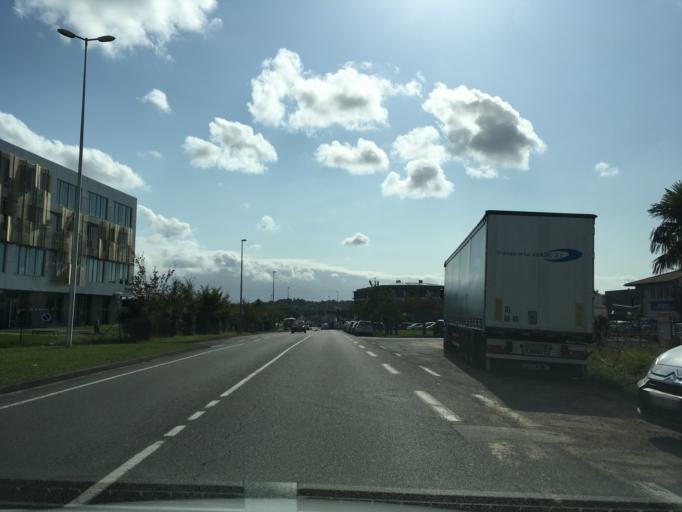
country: FR
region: Aquitaine
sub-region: Departement des Pyrenees-Atlantiques
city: Bayonne
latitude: 43.4687
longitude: -1.4905
